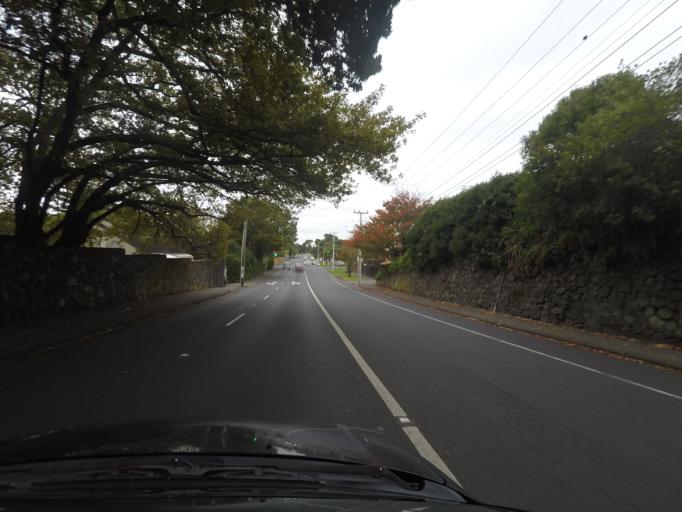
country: NZ
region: Auckland
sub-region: Auckland
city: Auckland
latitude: -36.8819
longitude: 174.7718
